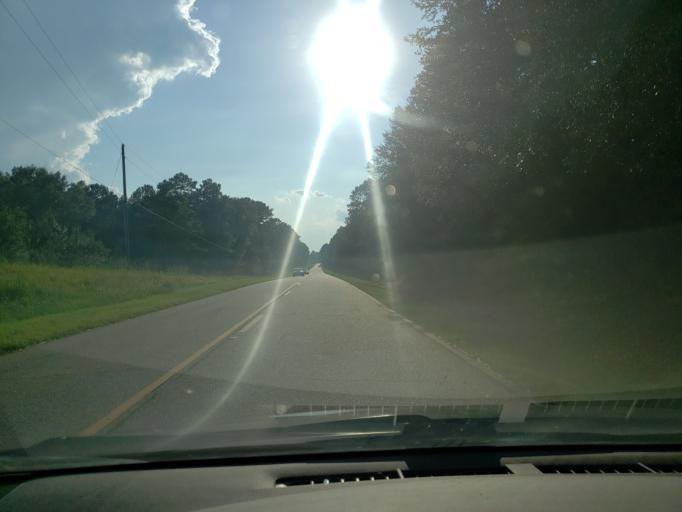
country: US
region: Georgia
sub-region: Terrell County
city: Dawson
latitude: 31.5774
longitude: -84.3834
